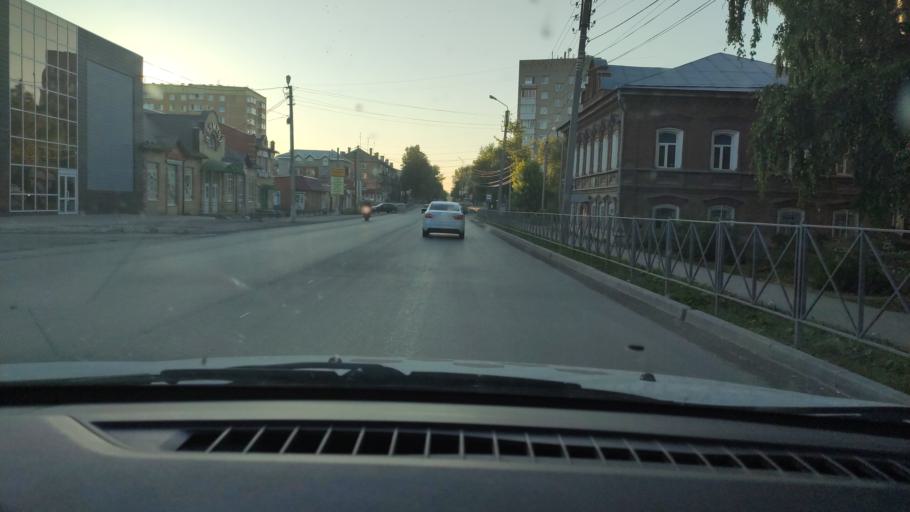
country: RU
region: Perm
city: Kungur
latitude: 57.4341
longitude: 56.9369
